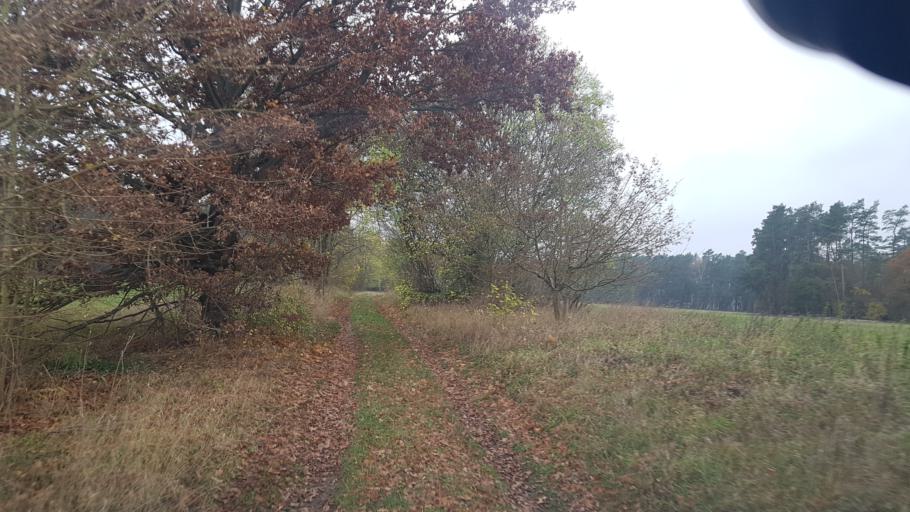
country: DE
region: Brandenburg
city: Lindow
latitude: 52.9351
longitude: 13.0641
